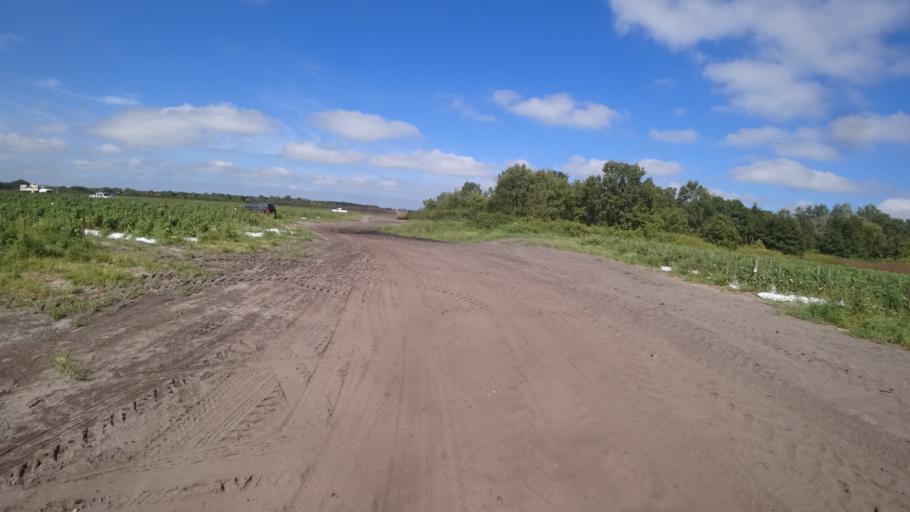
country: US
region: Florida
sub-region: DeSoto County
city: Arcadia
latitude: 27.2847
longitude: -82.0785
